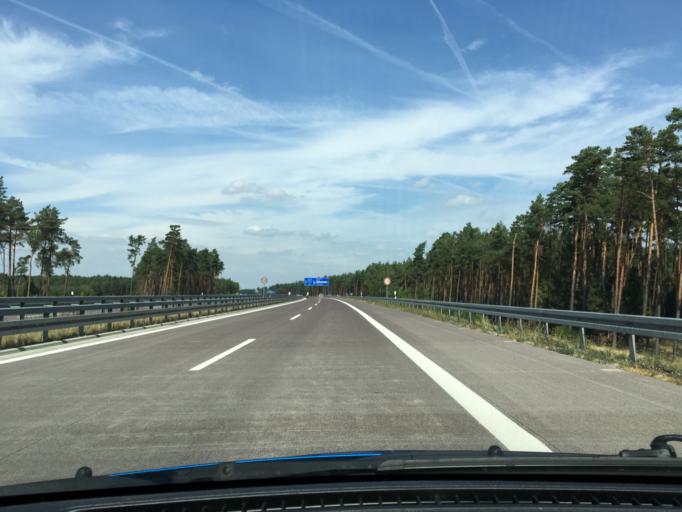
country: DE
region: Mecklenburg-Vorpommern
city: Gross Laasch
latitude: 53.4054
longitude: 11.5312
